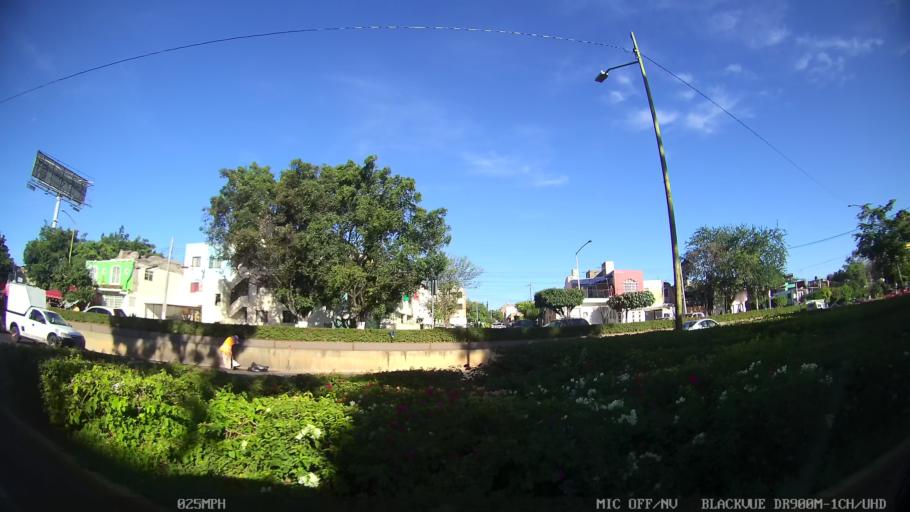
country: MX
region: Jalisco
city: Tlaquepaque
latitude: 20.6787
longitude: -103.2944
